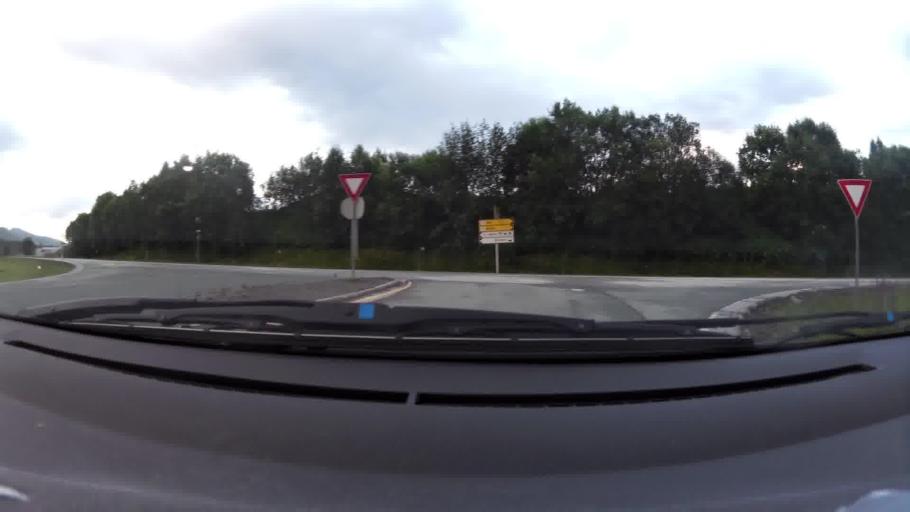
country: NO
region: More og Romsdal
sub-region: Molde
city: Molde
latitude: 62.7667
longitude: 7.2771
